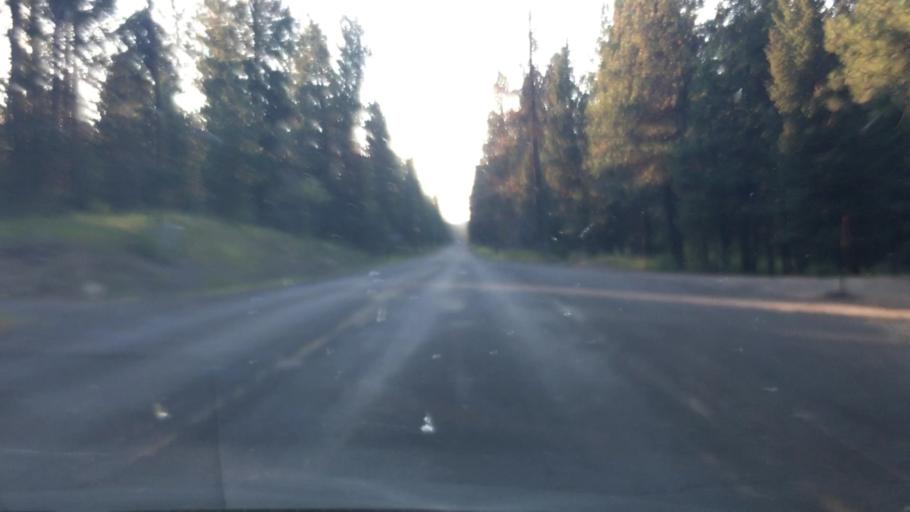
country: US
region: Idaho
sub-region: Valley County
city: McCall
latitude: 44.9177
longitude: -116.1345
